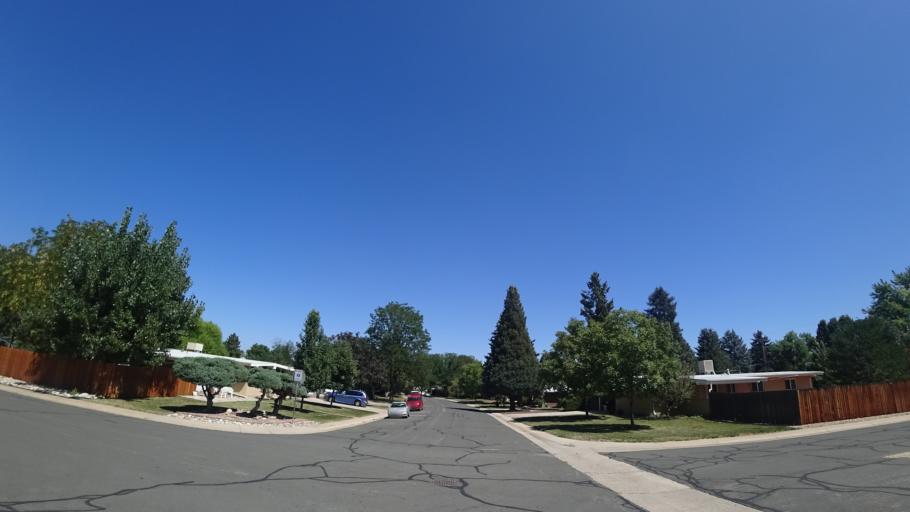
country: US
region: Colorado
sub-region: Arapahoe County
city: Greenwood Village
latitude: 39.6072
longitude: -104.9561
